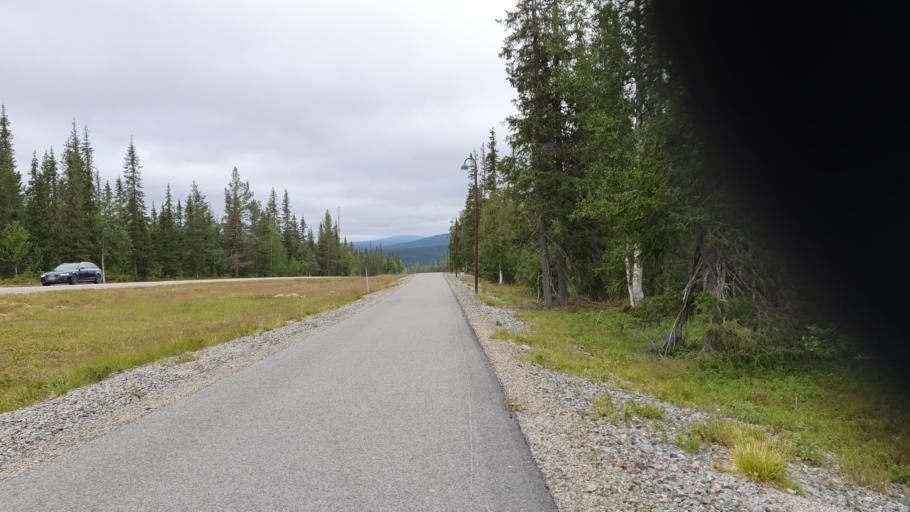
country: FI
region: Lapland
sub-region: Tunturi-Lappi
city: Kolari
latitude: 67.5864
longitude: 24.2019
